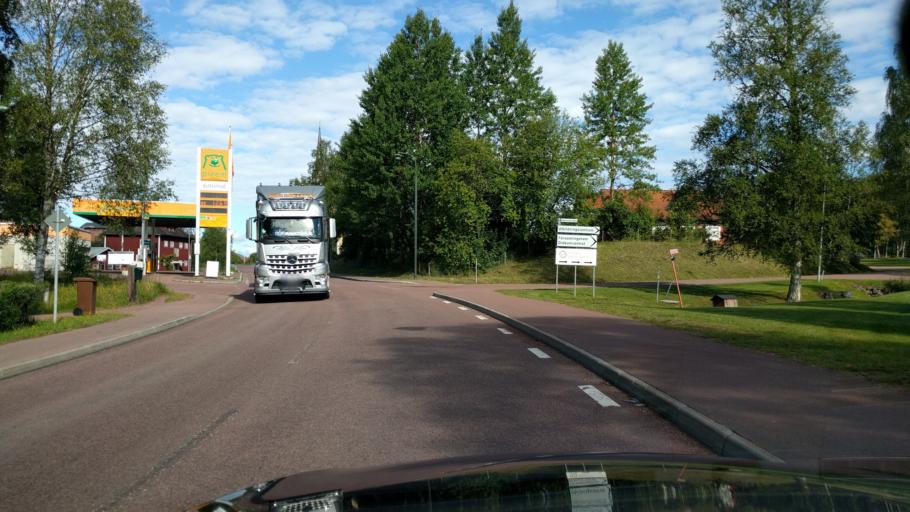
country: SE
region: Dalarna
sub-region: Alvdalens Kommun
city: AElvdalen
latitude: 61.2243
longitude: 14.0446
